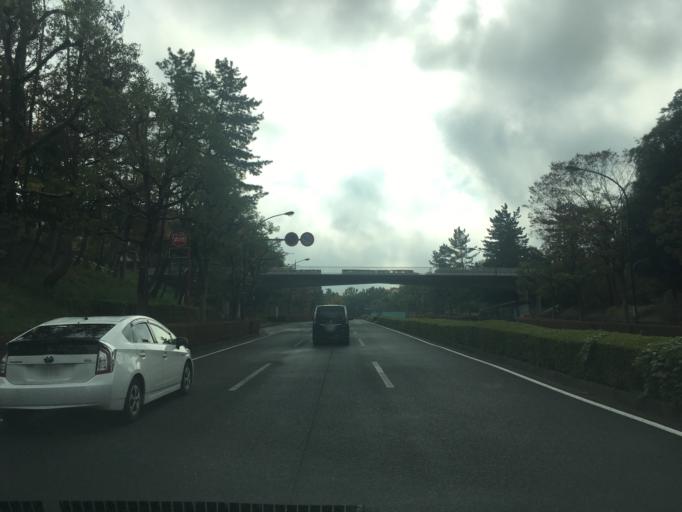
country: JP
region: Tokyo
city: Hino
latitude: 35.6171
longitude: 139.4222
